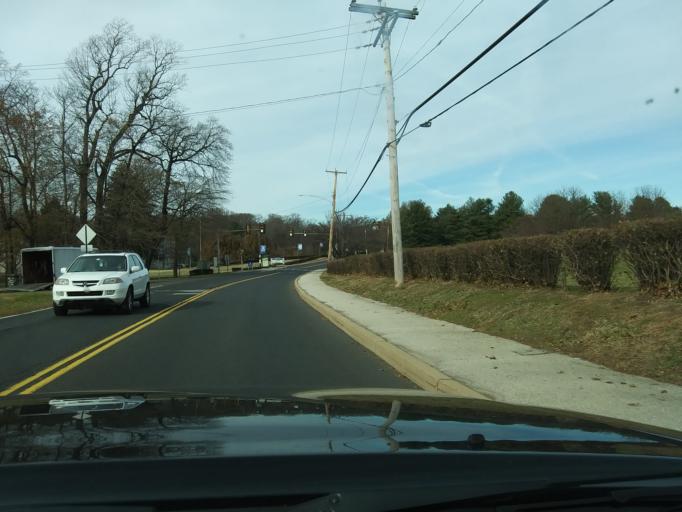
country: US
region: Pennsylvania
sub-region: Montgomery County
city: Rockledge
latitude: 40.0871
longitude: -75.1026
